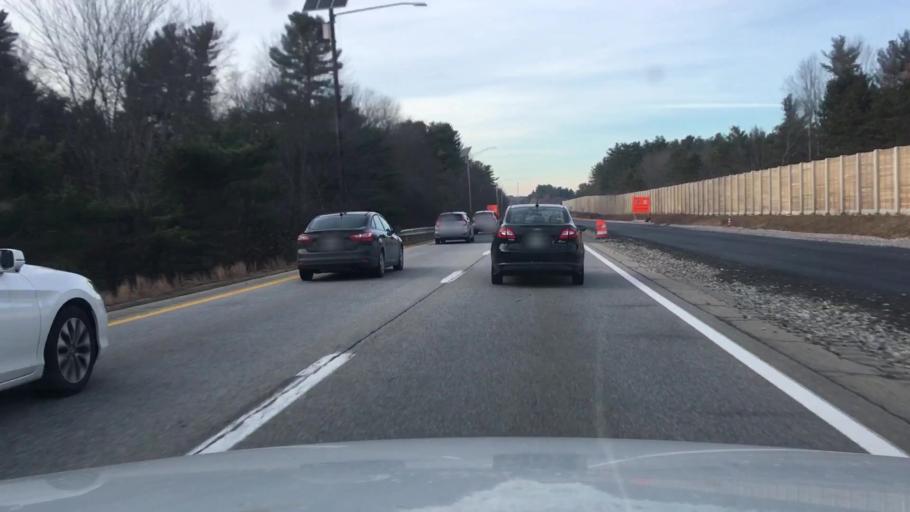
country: US
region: New Hampshire
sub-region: Rockingham County
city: Auburn
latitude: 42.9481
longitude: -71.3947
